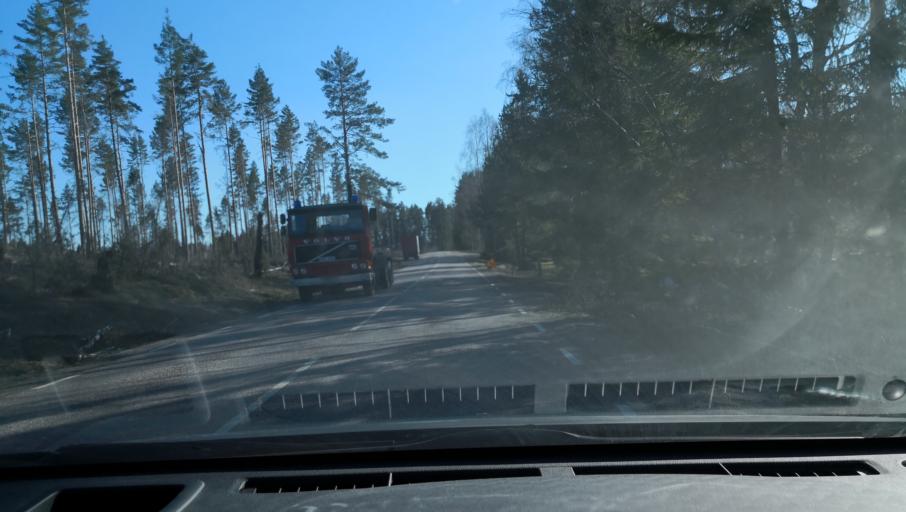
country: SE
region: Dalarna
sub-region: Avesta Kommun
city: Avesta
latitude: 59.9987
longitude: 16.3472
